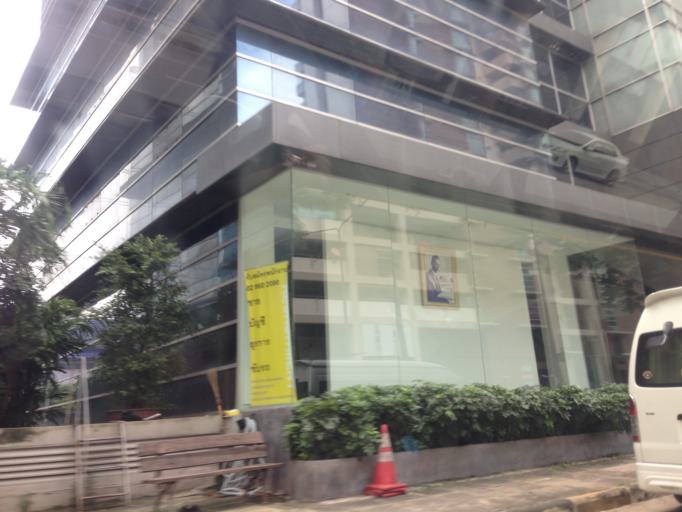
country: TH
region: Nonthaburi
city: Pak Kret
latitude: 13.9267
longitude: 100.5337
